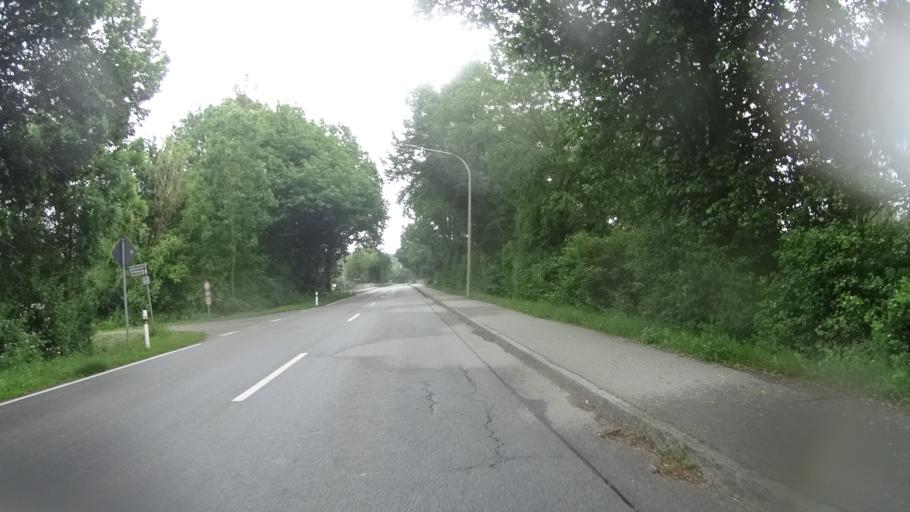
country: DE
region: Bavaria
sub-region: Lower Bavaria
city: Hebertsfelden
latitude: 48.4132
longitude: 12.8174
